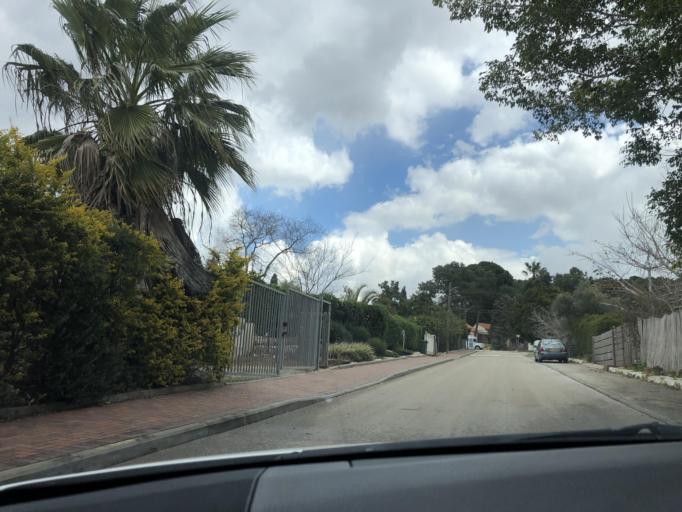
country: IL
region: Central District
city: Tel Mond
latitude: 32.2651
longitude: 34.9298
